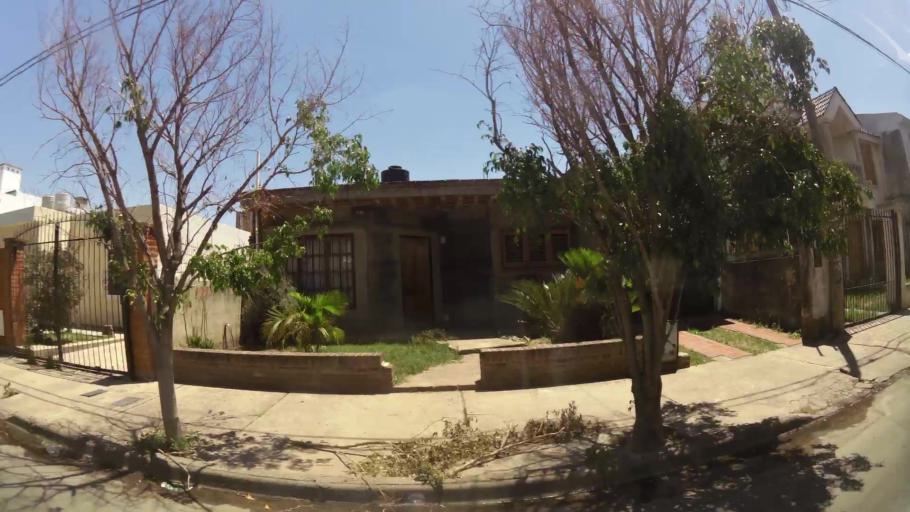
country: AR
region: Cordoba
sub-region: Departamento de Capital
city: Cordoba
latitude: -31.3800
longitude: -64.1399
